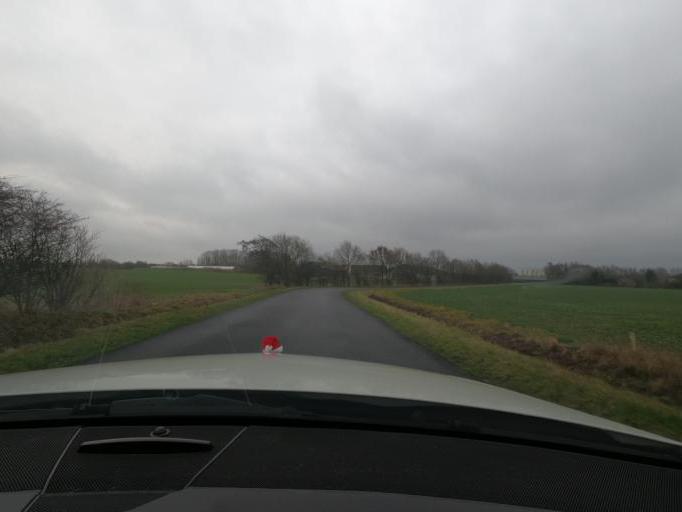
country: DK
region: South Denmark
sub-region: Haderslev Kommune
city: Starup
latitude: 55.2524
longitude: 9.6852
